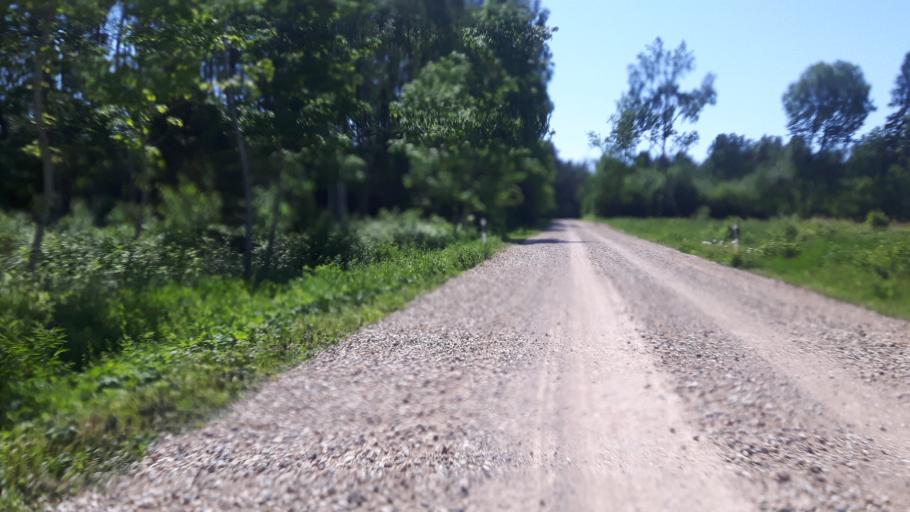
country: EE
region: Paernumaa
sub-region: Tootsi vald
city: Tootsi
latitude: 58.5107
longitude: 24.9086
